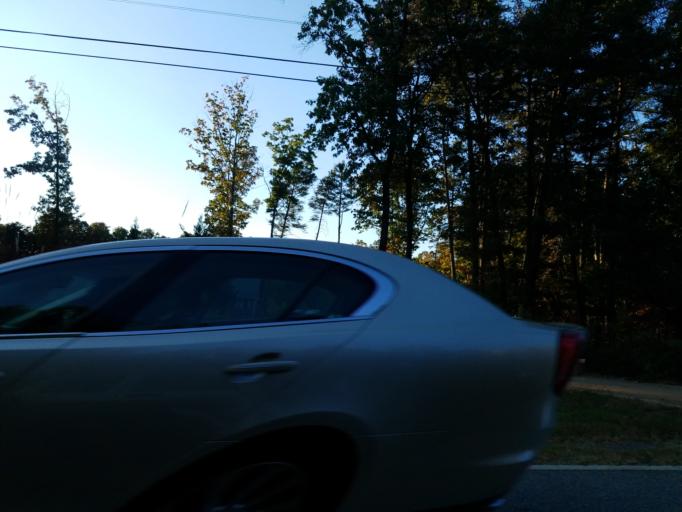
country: US
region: Georgia
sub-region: Dawson County
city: Dawsonville
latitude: 34.5430
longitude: -84.1642
